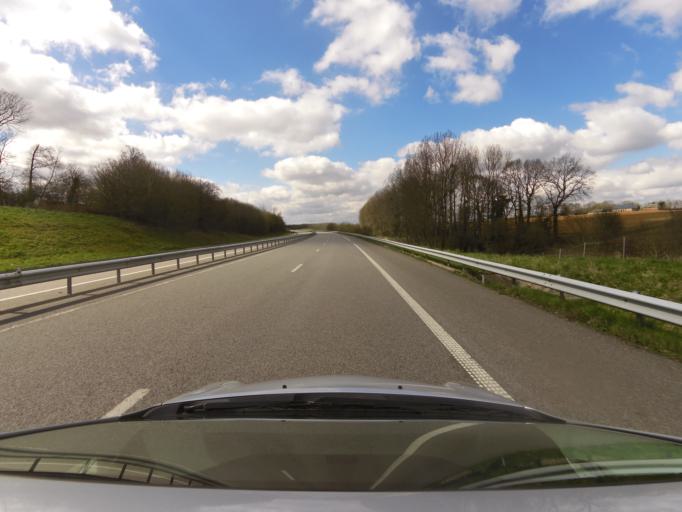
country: FR
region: Haute-Normandie
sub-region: Departement de la Seine-Maritime
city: Yerville
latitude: 49.6634
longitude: 0.9256
